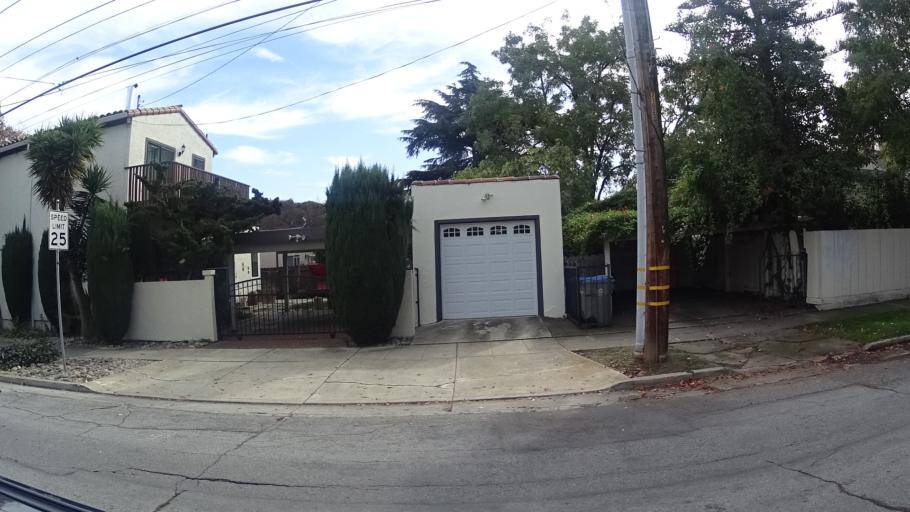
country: US
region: California
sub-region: Santa Clara County
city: Burbank
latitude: 37.3403
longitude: -121.9308
